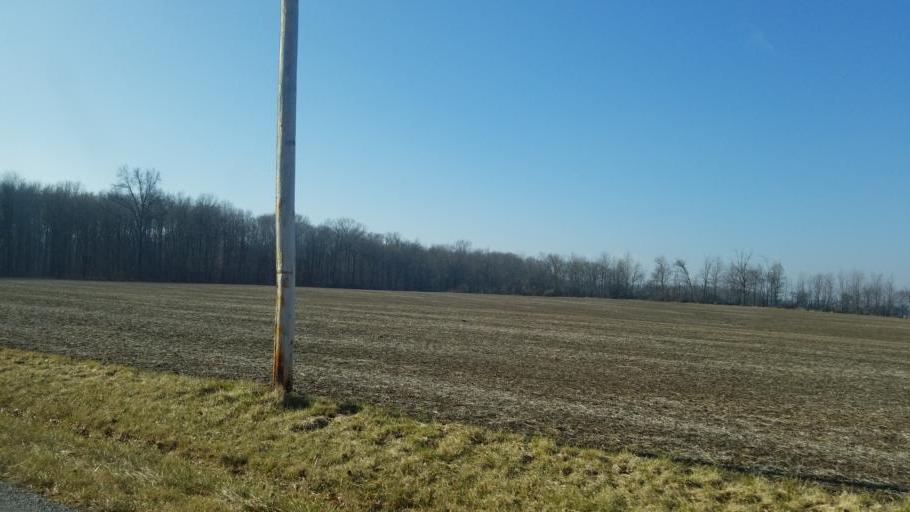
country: US
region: Ohio
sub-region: Seneca County
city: Tiffin
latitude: 41.1201
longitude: -83.1120
